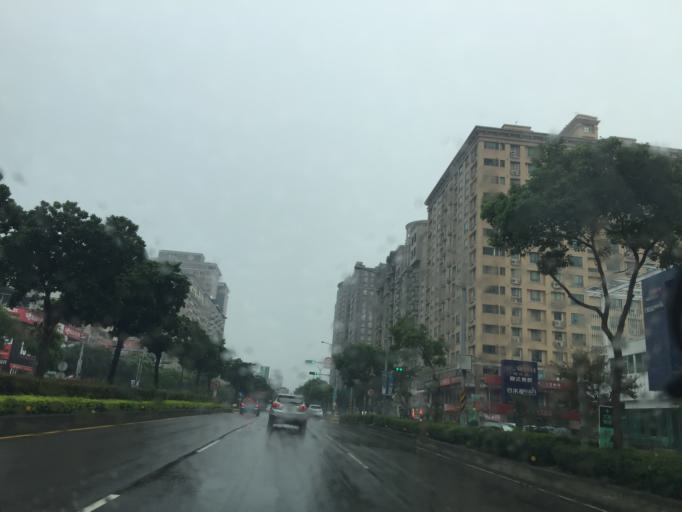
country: TW
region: Taiwan
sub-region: Hsinchu
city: Zhubei
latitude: 24.8213
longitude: 121.0236
